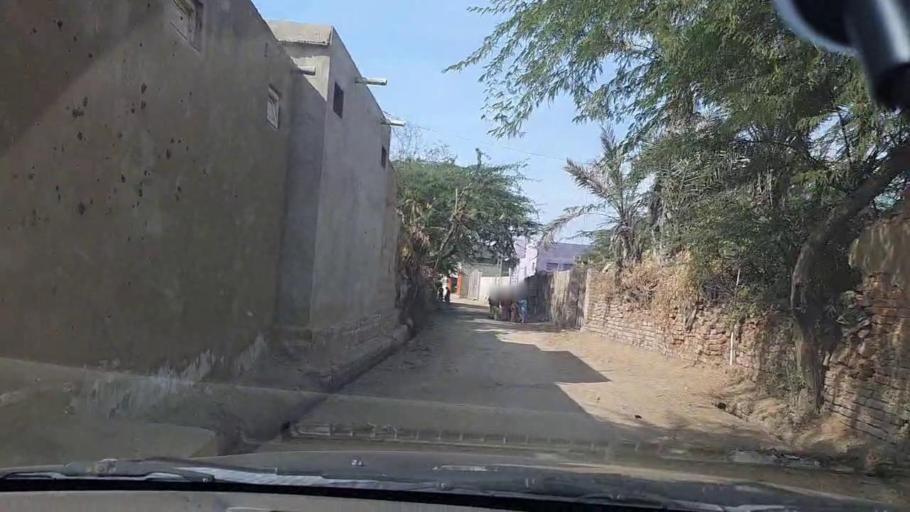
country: PK
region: Sindh
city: Mirpur Batoro
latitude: 24.7318
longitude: 68.2638
